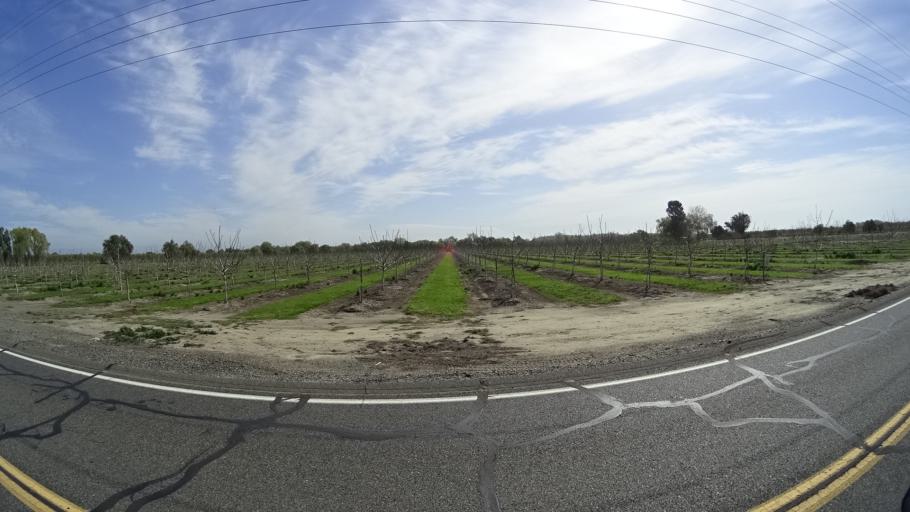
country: US
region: California
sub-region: Glenn County
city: Hamilton City
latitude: 39.6679
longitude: -122.0086
